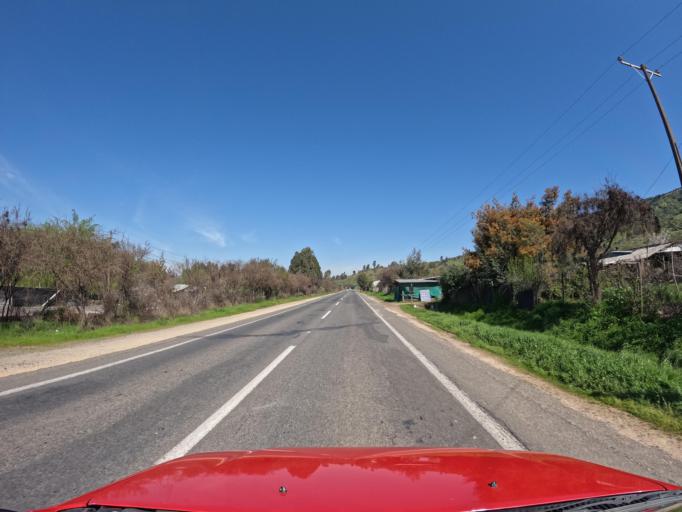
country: CL
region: Maule
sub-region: Provincia de Talca
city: Talca
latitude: -35.0825
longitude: -71.6399
